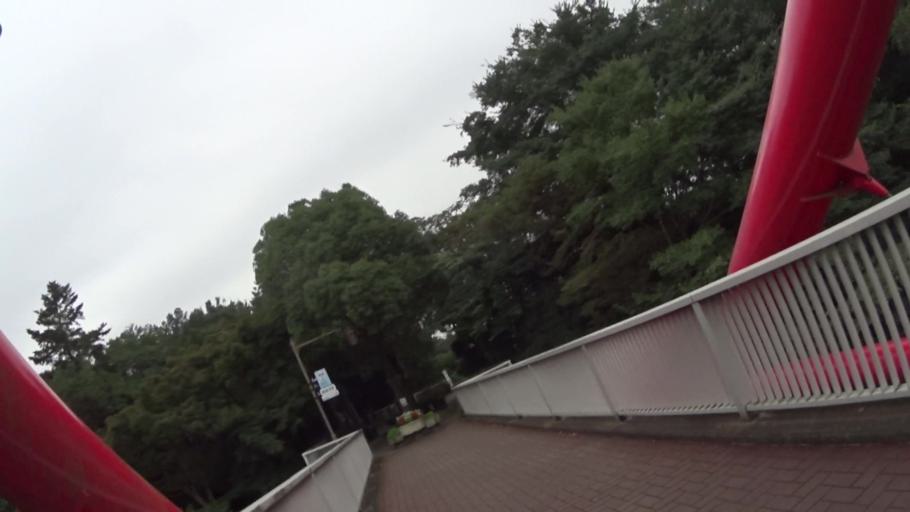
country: JP
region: Saitama
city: Hanno
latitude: 35.8541
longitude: 139.3105
